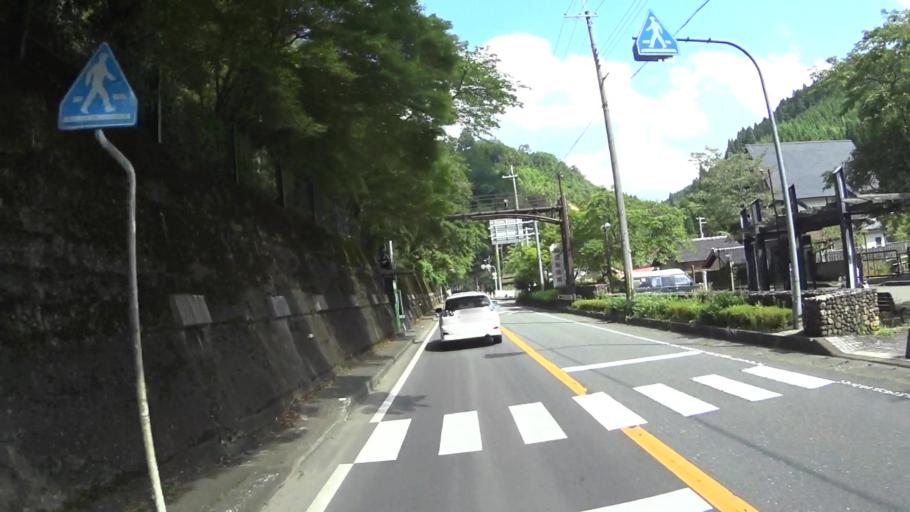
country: JP
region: Kyoto
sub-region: Kyoto-shi
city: Kamigyo-ku
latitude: 35.1203
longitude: 135.6525
